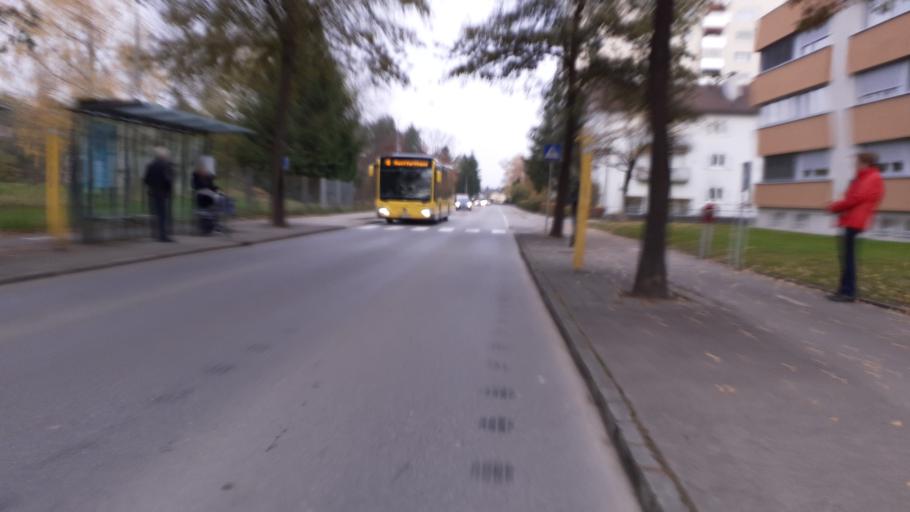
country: AT
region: Vorarlberg
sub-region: Politischer Bezirk Feldkirch
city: Nofels
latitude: 47.2502
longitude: 9.5879
